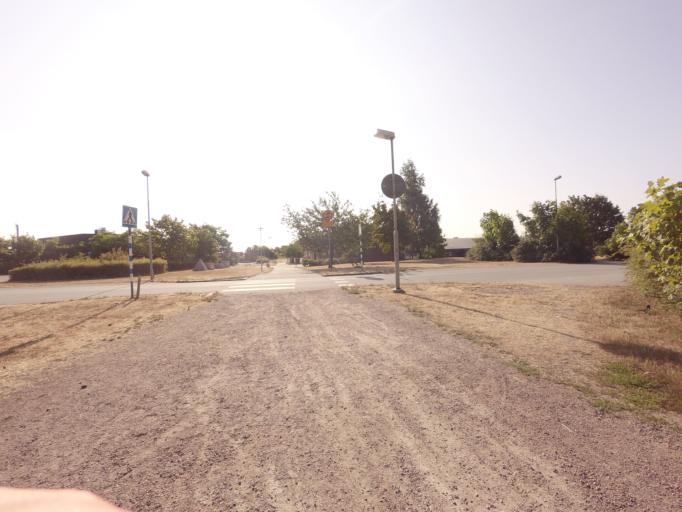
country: SE
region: Skane
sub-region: Landskrona
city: Asmundtorp
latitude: 55.8504
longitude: 12.9228
